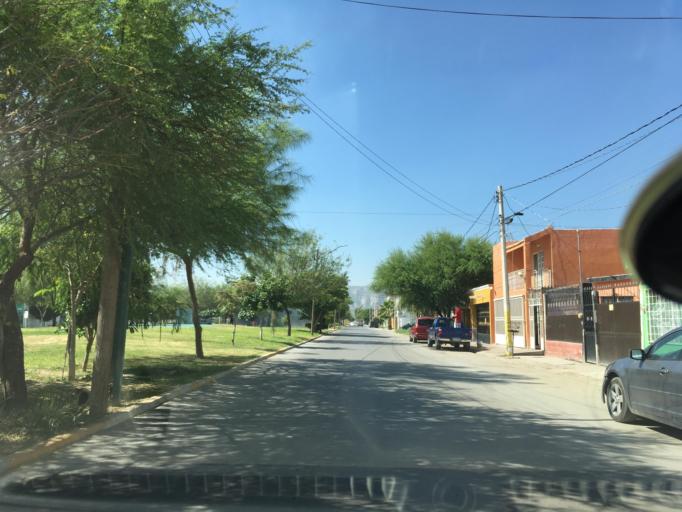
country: MX
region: Coahuila
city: Torreon
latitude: 25.5189
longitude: -103.3821
